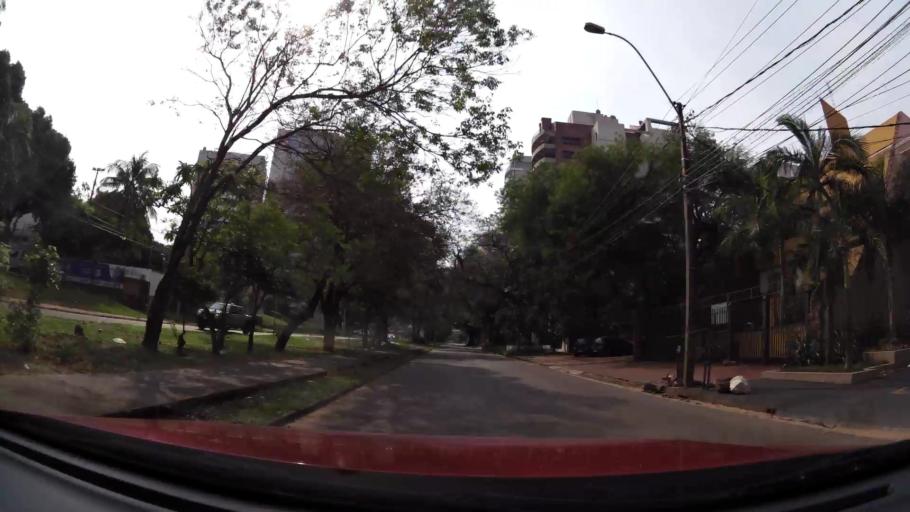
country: PY
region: Central
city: Fernando de la Mora
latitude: -25.2869
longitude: -57.5574
